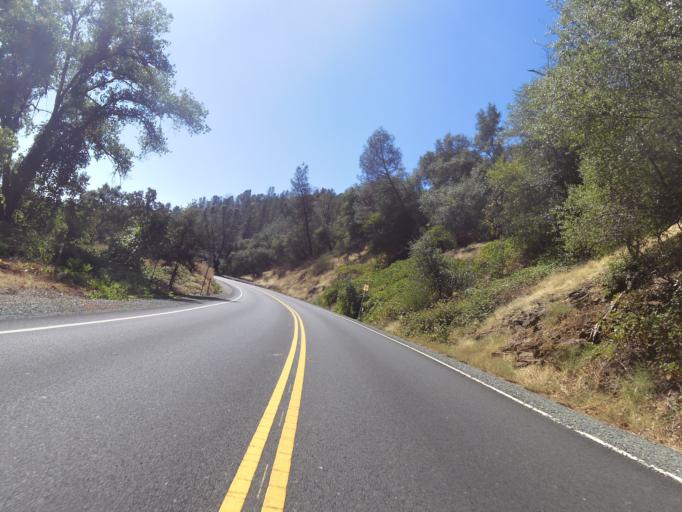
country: US
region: California
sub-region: Amador County
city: Plymouth
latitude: 38.5525
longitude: -120.8496
